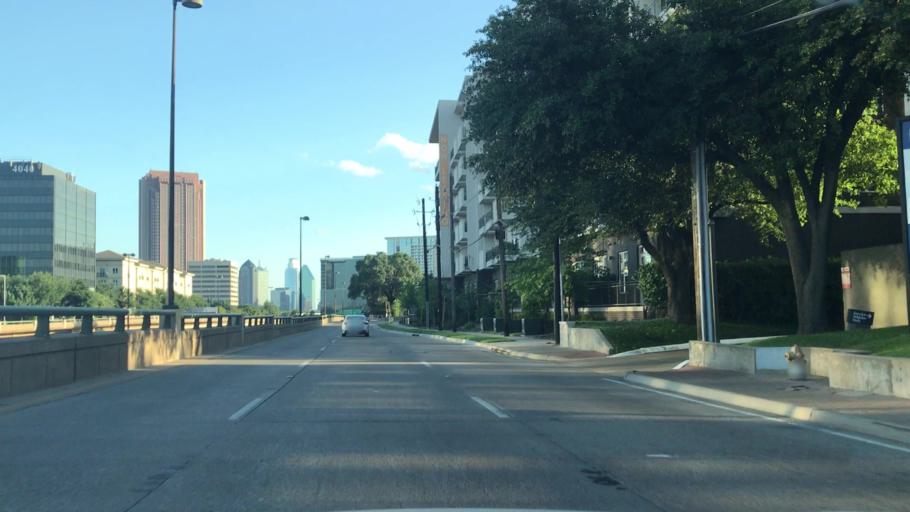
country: US
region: Texas
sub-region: Dallas County
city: Highland Park
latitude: 32.8147
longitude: -96.7903
